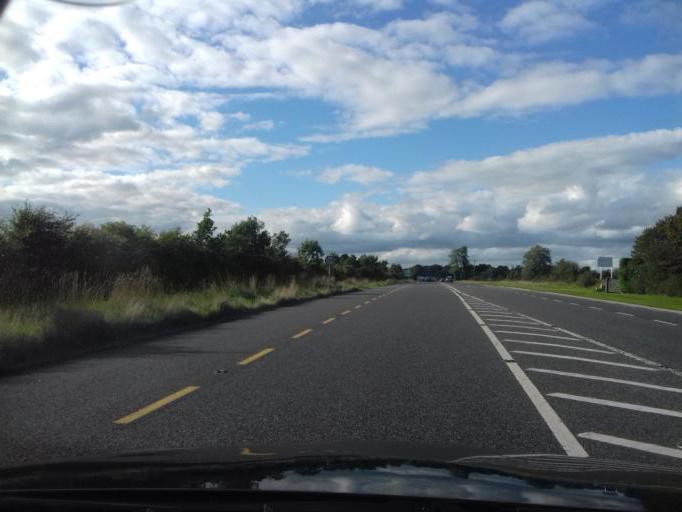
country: IE
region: Leinster
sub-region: Uibh Fhaili
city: Tullamore
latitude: 53.3067
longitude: -7.4946
